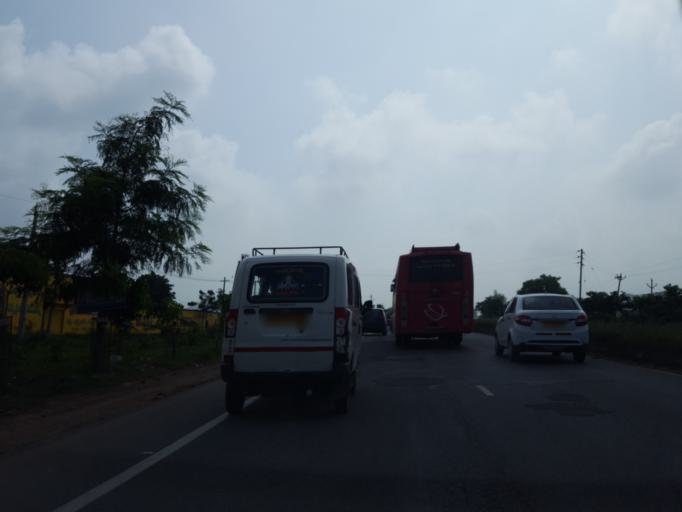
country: IN
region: Telangana
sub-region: Rangareddi
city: Ghatkesar
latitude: 17.2913
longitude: 78.7632
